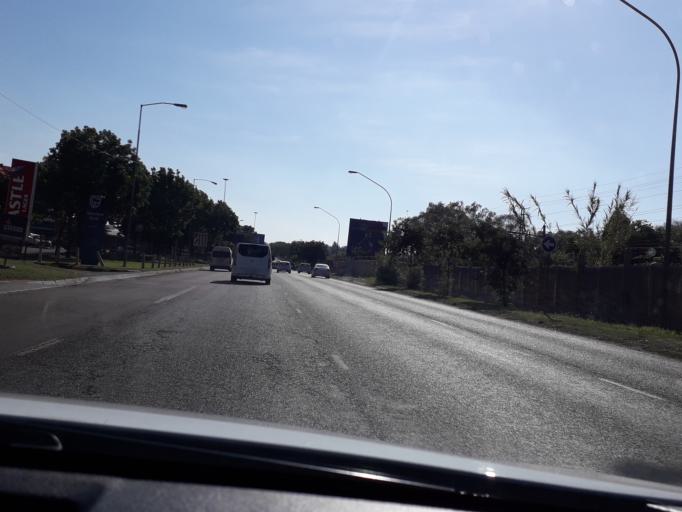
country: ZA
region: Gauteng
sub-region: City of Tshwane Metropolitan Municipality
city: Pretoria
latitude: -25.7450
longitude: 28.2451
